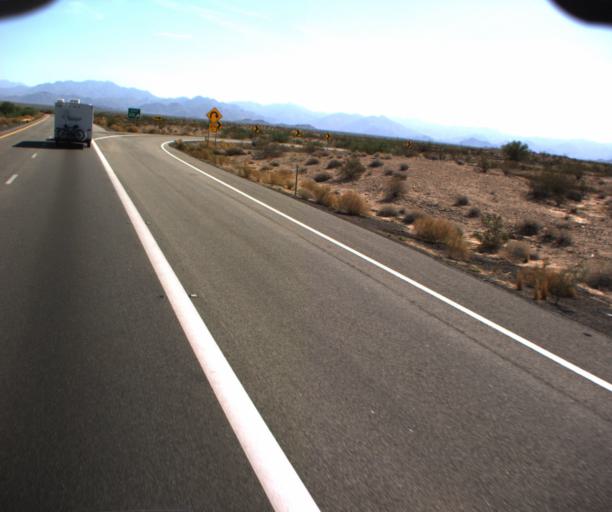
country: US
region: Arizona
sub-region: Mohave County
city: Desert Hills
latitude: 34.7949
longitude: -114.1604
